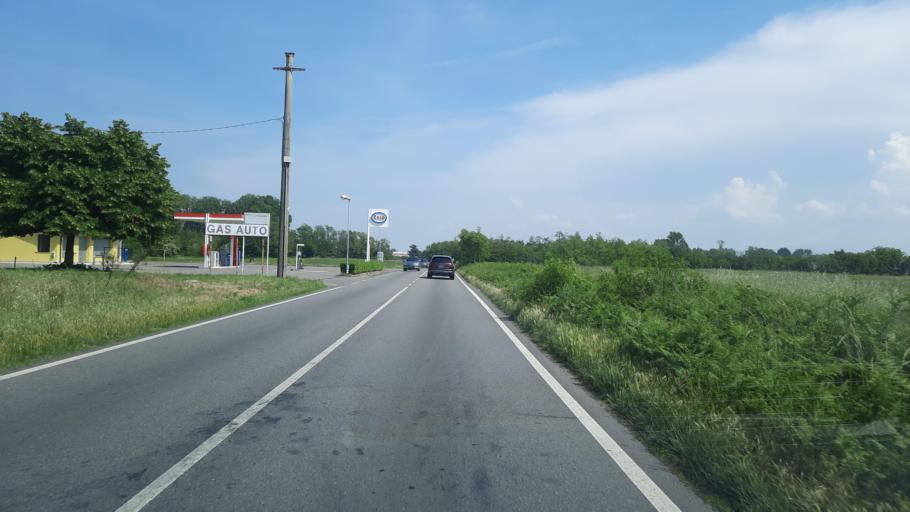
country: IT
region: Lombardy
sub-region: Provincia di Pavia
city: Villanova d'Ardenghi
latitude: 45.1631
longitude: 9.0248
